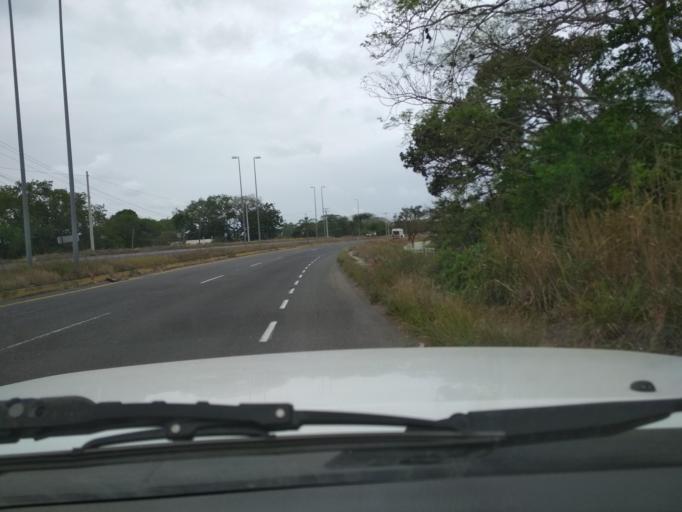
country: MX
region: Veracruz
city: El Tejar
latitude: 19.0674
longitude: -96.1312
